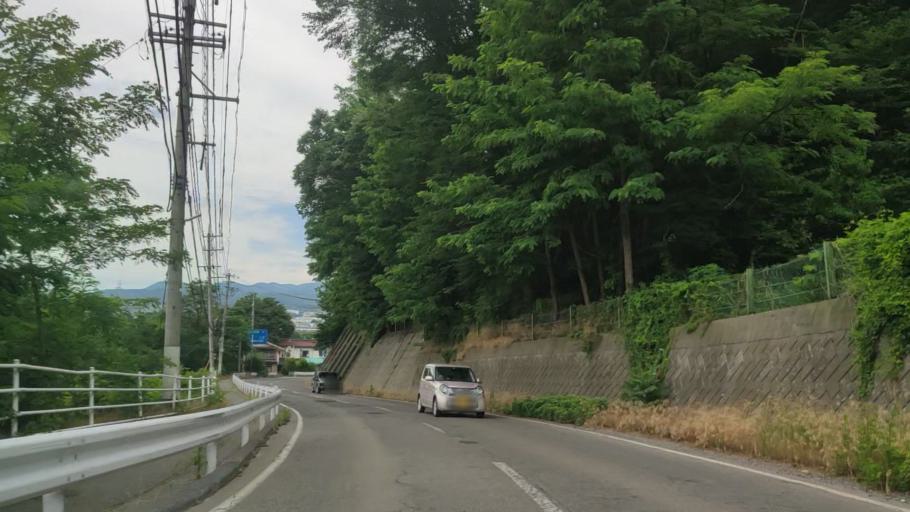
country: JP
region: Nagano
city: Kamimaruko
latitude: 36.3365
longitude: 138.3511
